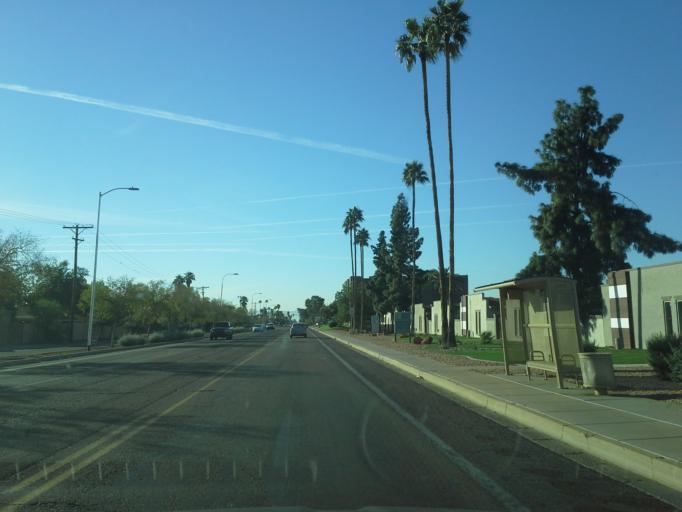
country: US
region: Arizona
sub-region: Maricopa County
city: Phoenix
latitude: 33.5127
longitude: -112.0913
